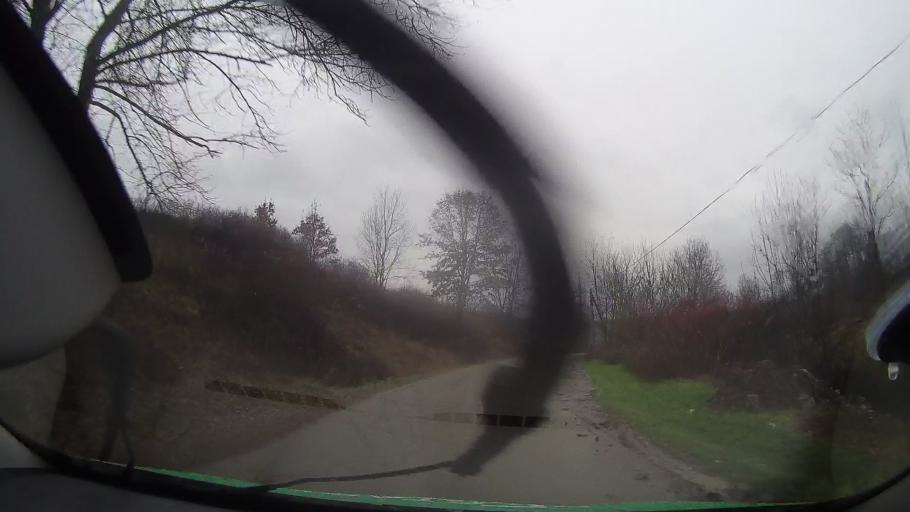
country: RO
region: Bihor
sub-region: Comuna Uileacu de Beius
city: Uileacu de Beius
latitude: 46.7028
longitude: 22.2201
